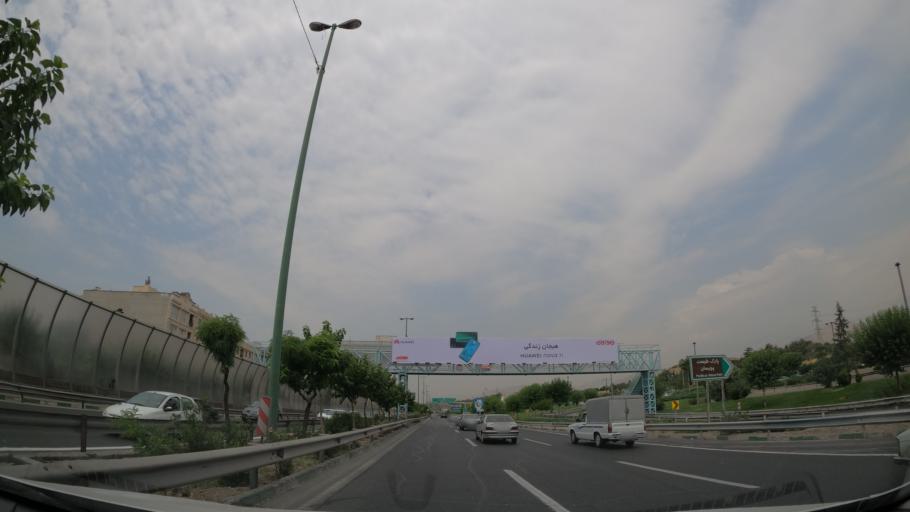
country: IR
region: Tehran
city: Tehran
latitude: 35.7393
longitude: 51.3578
